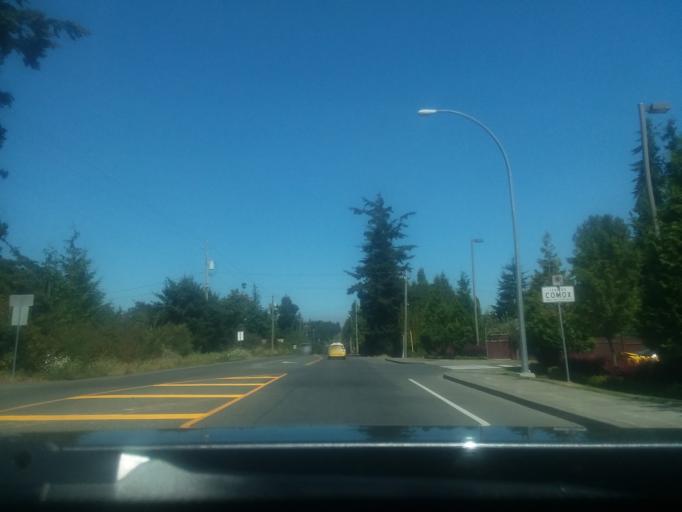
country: CA
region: British Columbia
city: Courtenay
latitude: 49.6892
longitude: -124.9348
